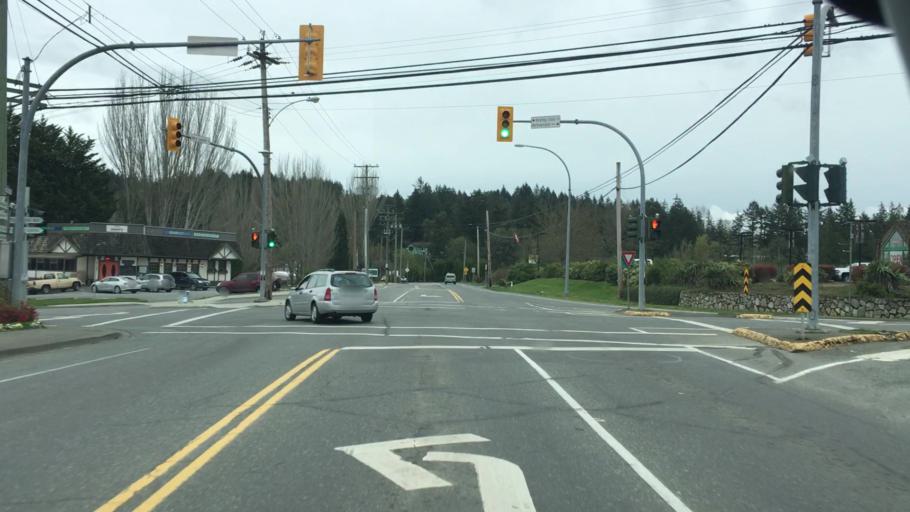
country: CA
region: British Columbia
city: North Saanich
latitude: 48.5654
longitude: -123.4387
